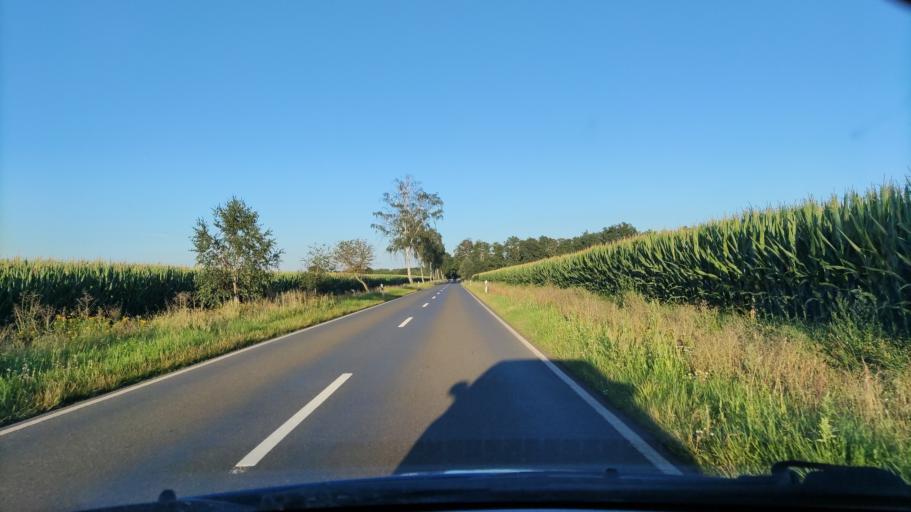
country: DE
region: Lower Saxony
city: Jameln
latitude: 53.0261
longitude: 11.1322
